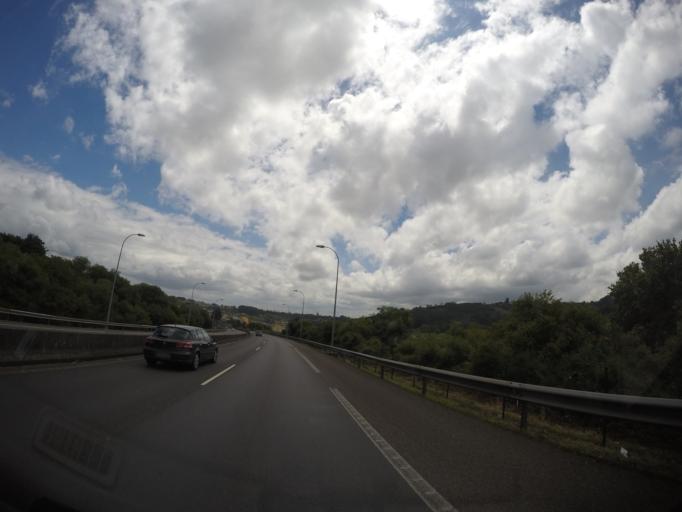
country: ES
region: Galicia
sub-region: Provincia da Coruna
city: Culleredo
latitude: 43.3169
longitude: -8.3911
